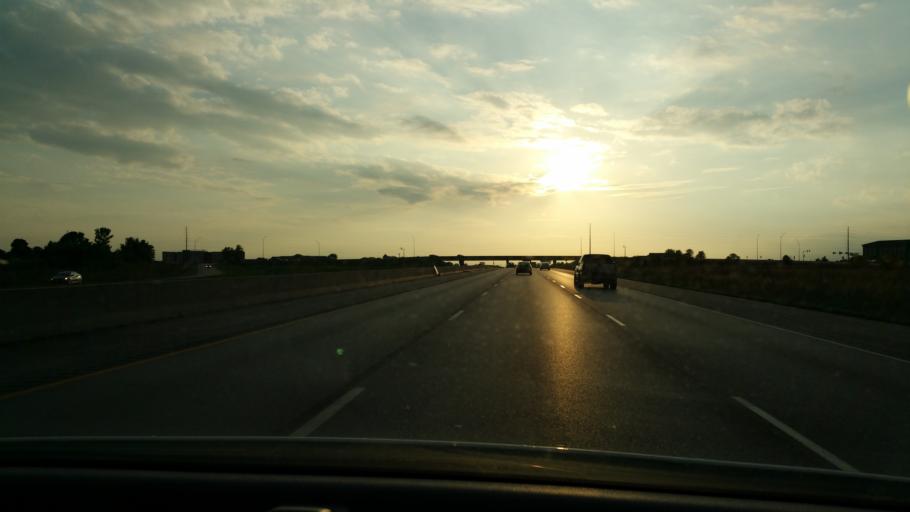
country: US
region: Iowa
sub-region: Polk County
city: Urbandale
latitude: 41.6524
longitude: -93.7308
